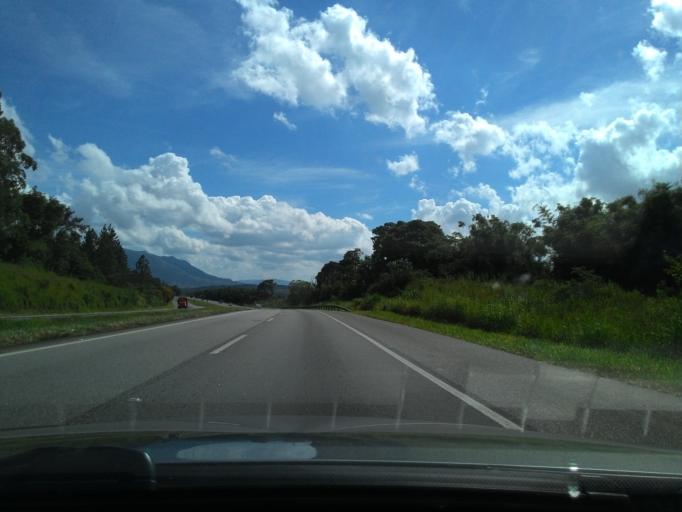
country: BR
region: Sao Paulo
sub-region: Jacupiranga
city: Jacupiranga
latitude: -24.7165
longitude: -48.0356
